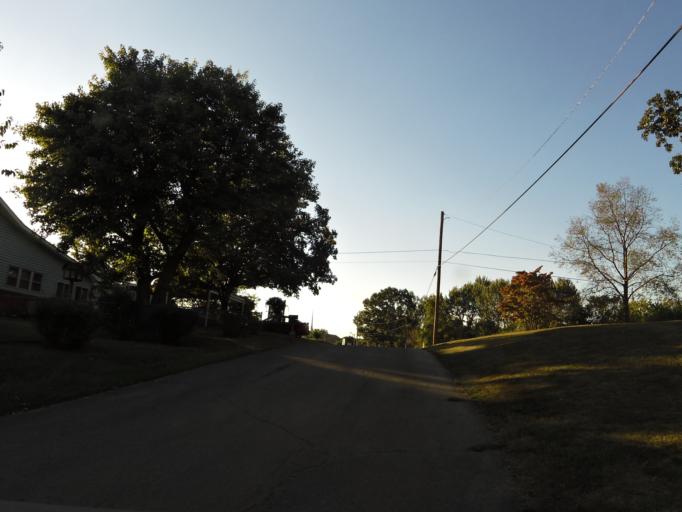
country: US
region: Tennessee
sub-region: Blount County
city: Alcoa
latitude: 35.7955
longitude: -83.9722
